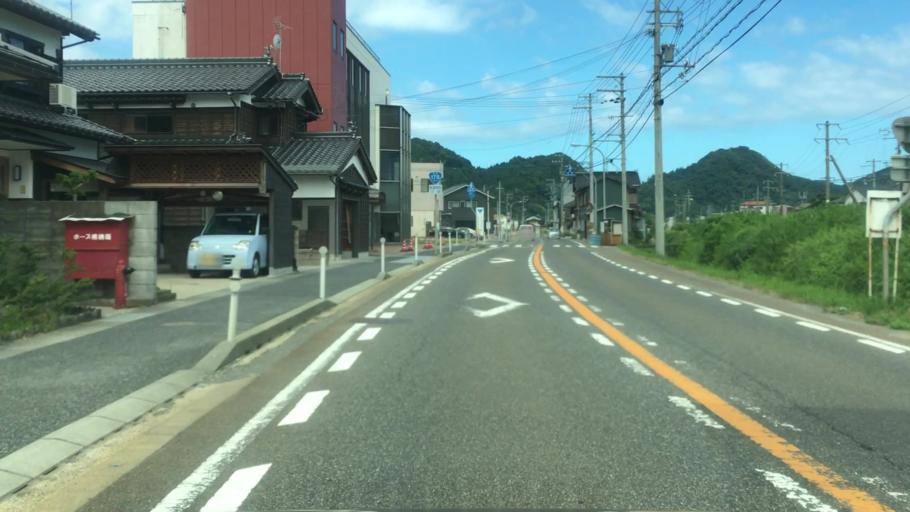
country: JP
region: Tottori
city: Tottori
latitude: 35.6191
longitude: 134.4571
